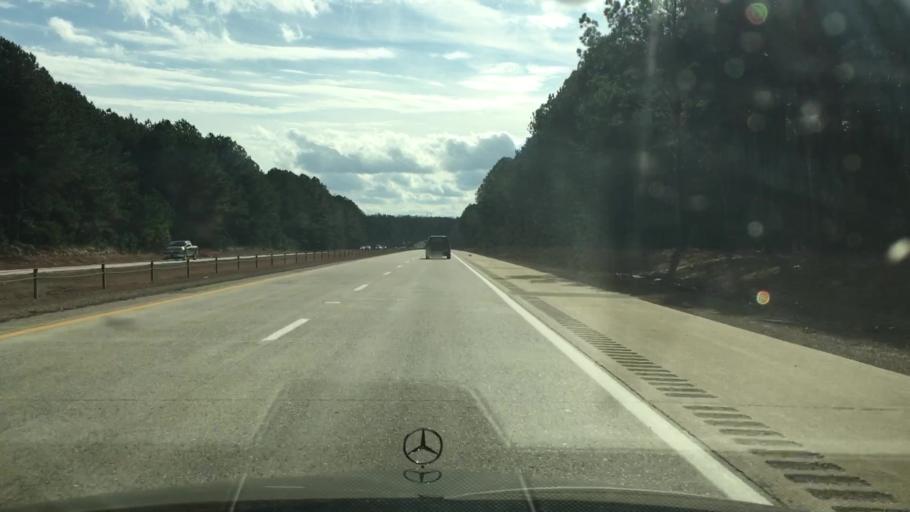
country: US
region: North Carolina
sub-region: Johnston County
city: Clayton
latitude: 35.5716
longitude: -78.5764
